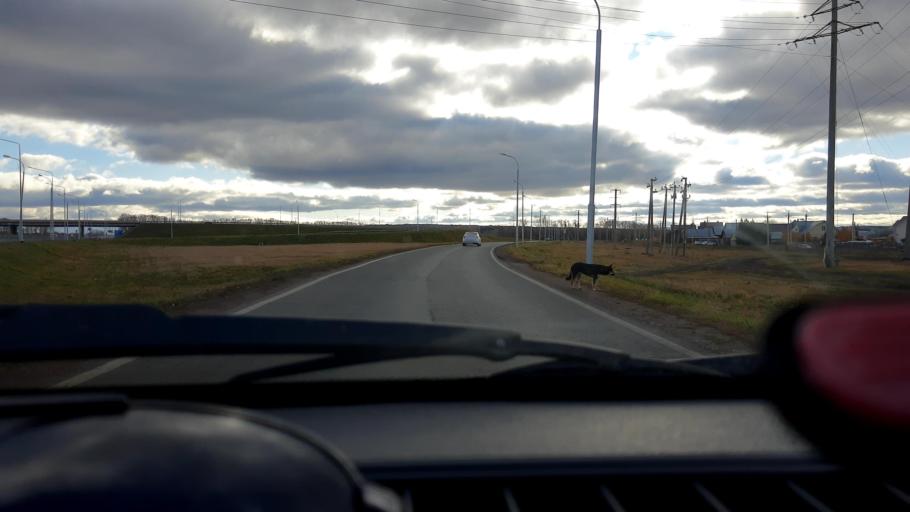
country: RU
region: Bashkortostan
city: Kabakovo
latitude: 54.4959
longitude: 55.9045
